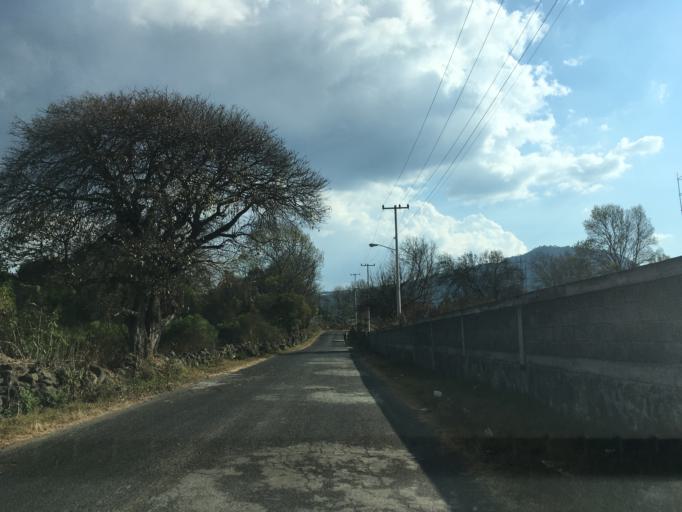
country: MX
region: Michoacan
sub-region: Patzcuaro
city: Santa Ana Chapitiro
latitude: 19.5403
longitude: -101.6395
